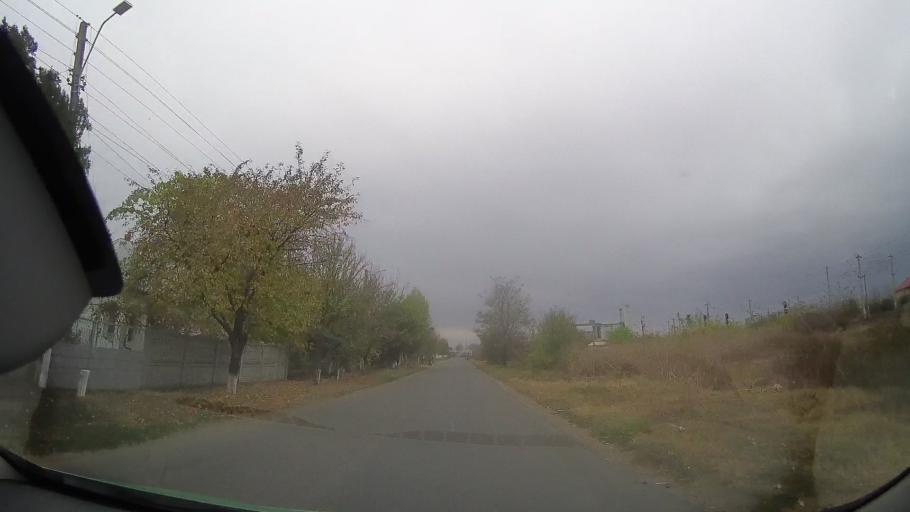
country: RO
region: Braila
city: Dudesti
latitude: 44.8893
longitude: 27.4354
